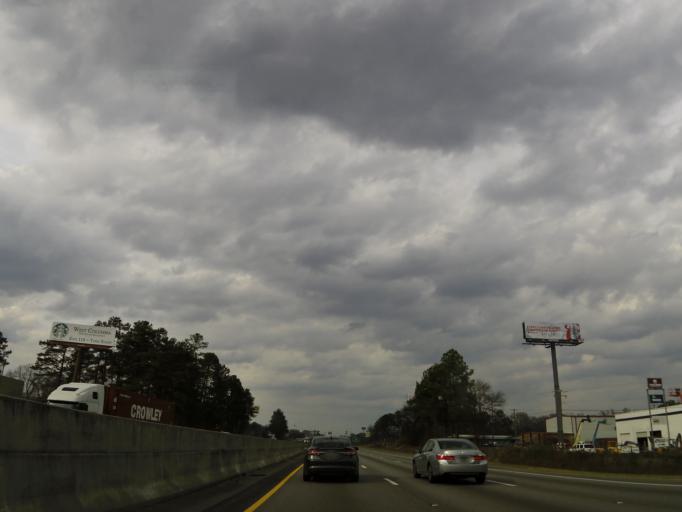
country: US
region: South Carolina
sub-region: Lexington County
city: West Columbia
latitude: 33.9940
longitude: -81.1078
